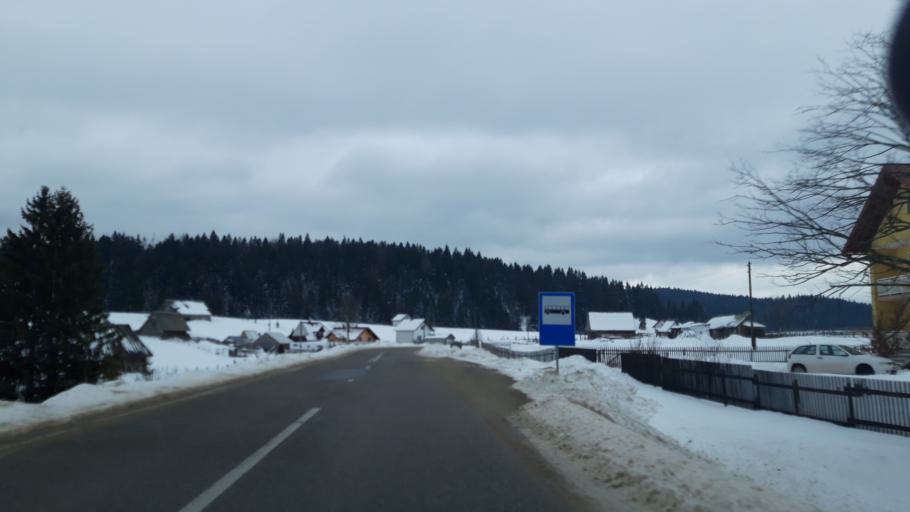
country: BA
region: Republika Srpska
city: Han Pijesak
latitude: 44.1083
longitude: 18.9698
